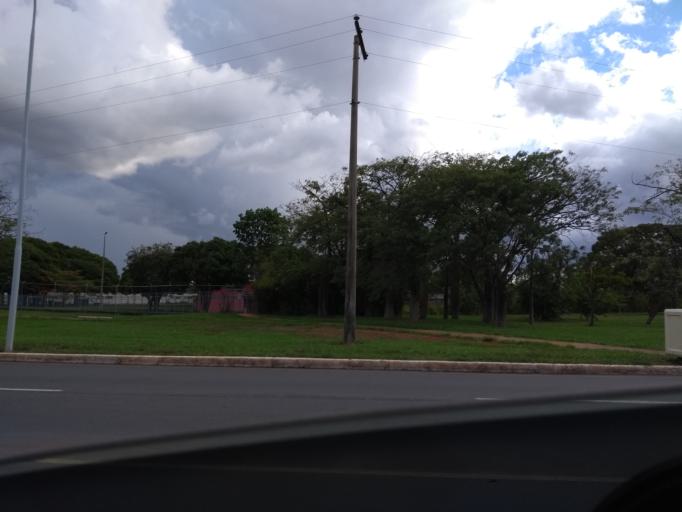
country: BR
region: Federal District
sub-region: Brasilia
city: Brasilia
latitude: -15.8040
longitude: -47.9090
